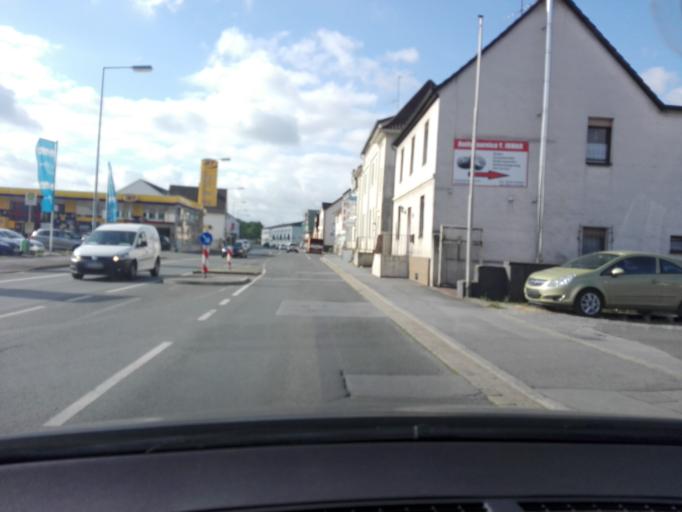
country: DE
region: North Rhine-Westphalia
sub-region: Regierungsbezirk Arnsberg
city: Menden
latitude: 51.4503
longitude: 7.7798
